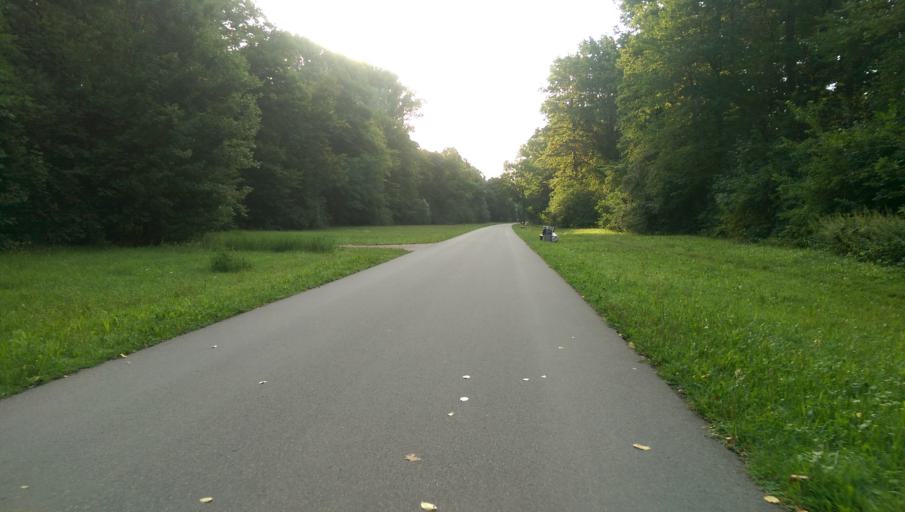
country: DE
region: Bavaria
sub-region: Regierungsbezirk Mittelfranken
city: Nuernberg
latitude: 49.4799
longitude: 11.0856
